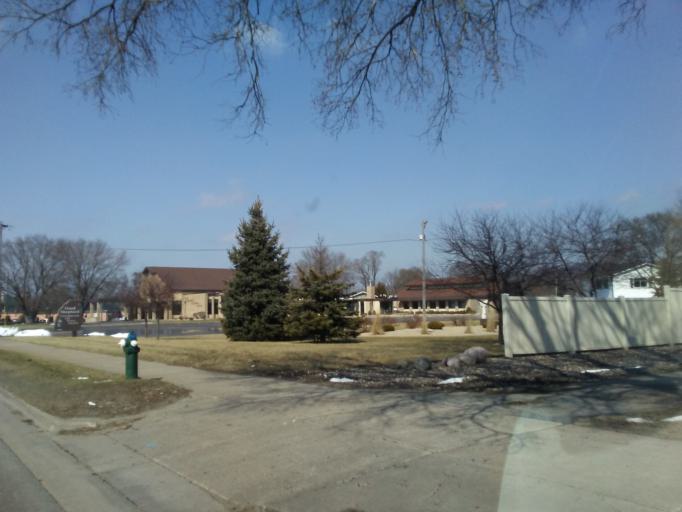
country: US
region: Wisconsin
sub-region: La Crosse County
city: La Crosse
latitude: 43.7720
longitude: -91.2165
